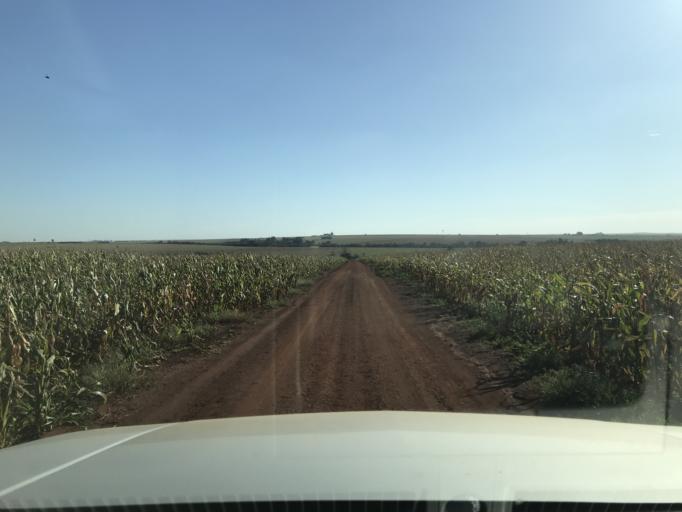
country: BR
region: Parana
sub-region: Palotina
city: Palotina
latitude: -24.2274
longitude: -53.8058
